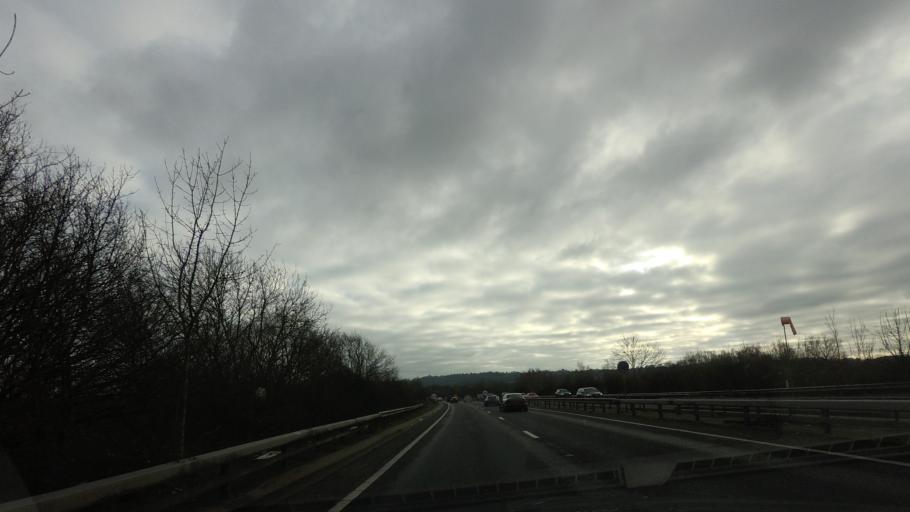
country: GB
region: England
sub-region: Kent
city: Tonbridge
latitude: 51.1897
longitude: 0.2357
